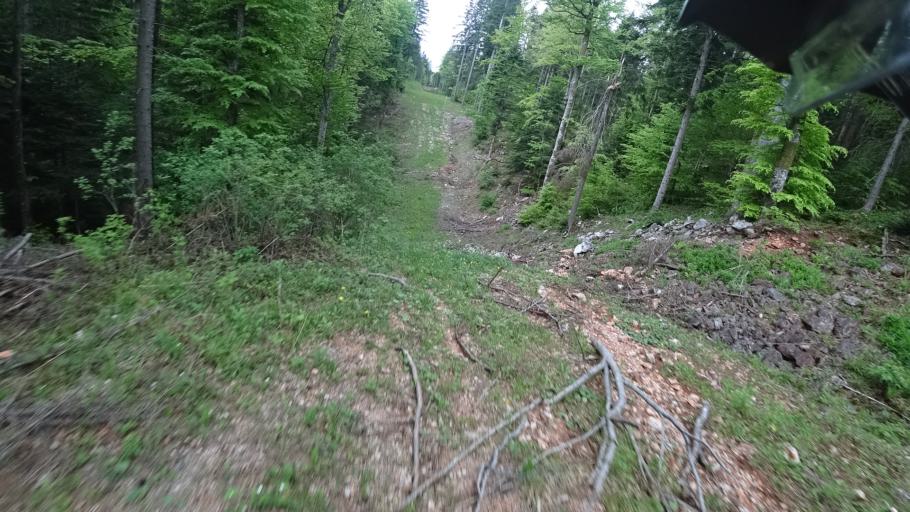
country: HR
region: Karlovacka
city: Plaski
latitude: 44.9540
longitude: 15.4151
